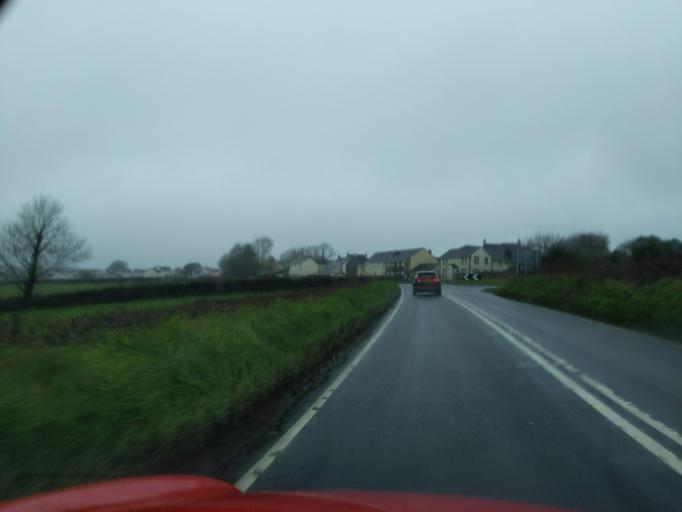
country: GB
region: England
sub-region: Cornwall
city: Launceston
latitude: 50.6268
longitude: -4.3401
